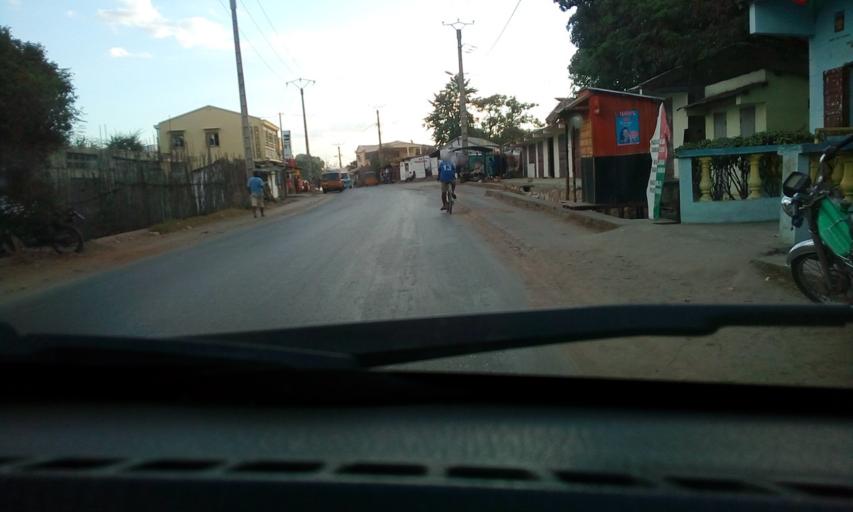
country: MG
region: Boeny
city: Mahajanga
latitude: -15.7153
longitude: 46.3366
